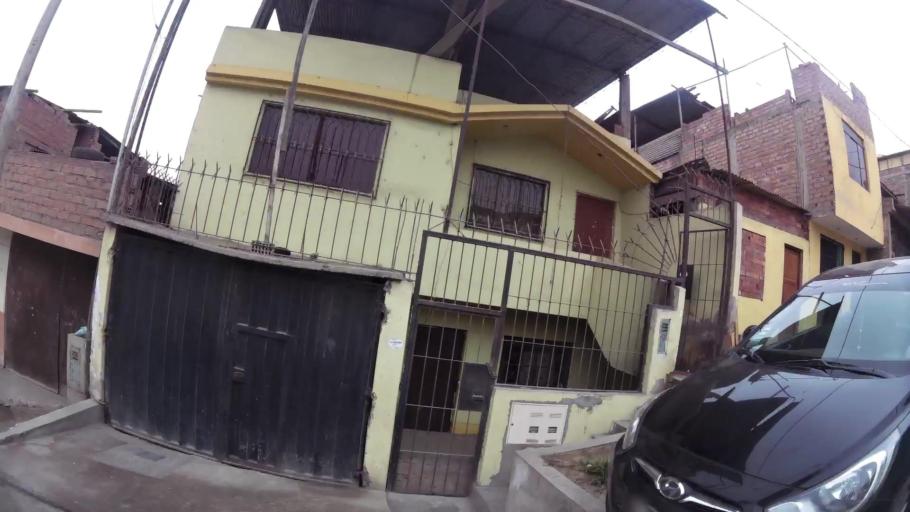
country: PE
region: Lima
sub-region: Lima
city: Surco
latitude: -12.1801
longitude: -76.9518
